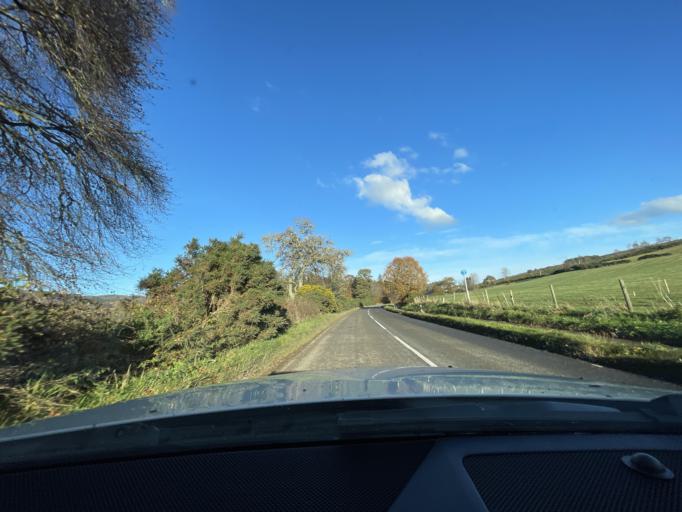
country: GB
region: Scotland
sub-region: Highland
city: Inverness
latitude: 57.3902
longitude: -4.3276
